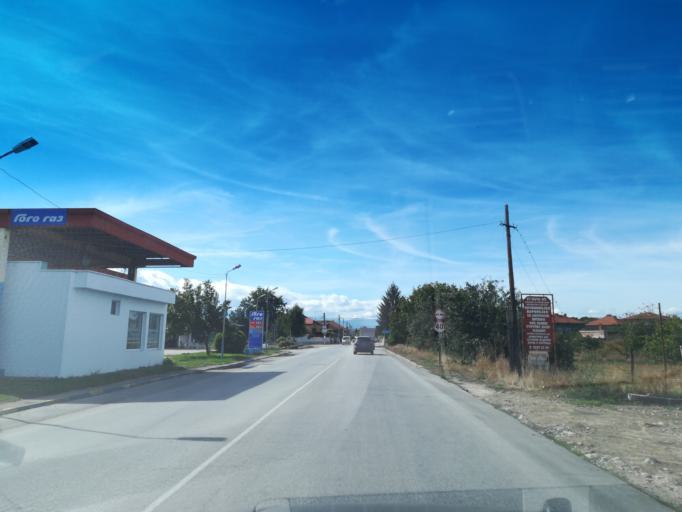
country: BG
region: Plovdiv
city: Stamboliyski
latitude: 42.1198
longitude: 24.5727
